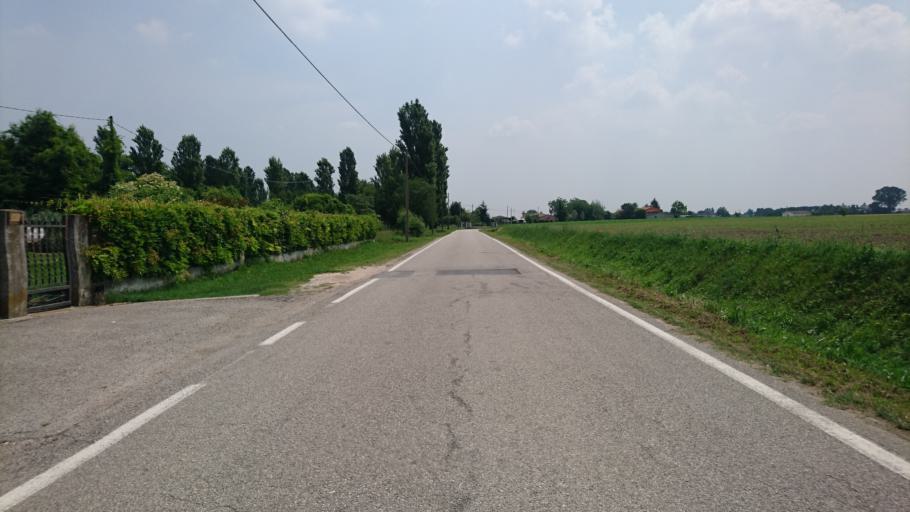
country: IT
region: Veneto
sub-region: Provincia di Padova
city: Cartura
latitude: 45.2624
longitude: 11.8812
